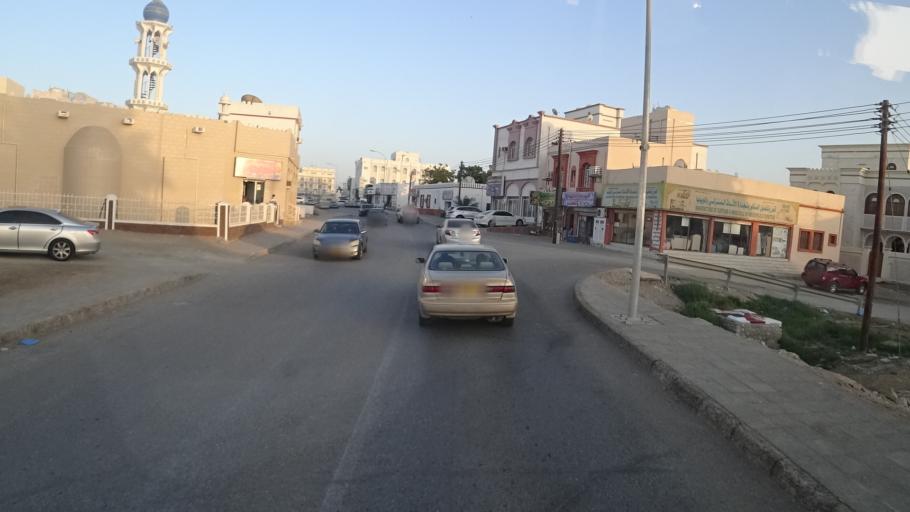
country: OM
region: Ash Sharqiyah
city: Sur
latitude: 22.5823
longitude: 59.5056
